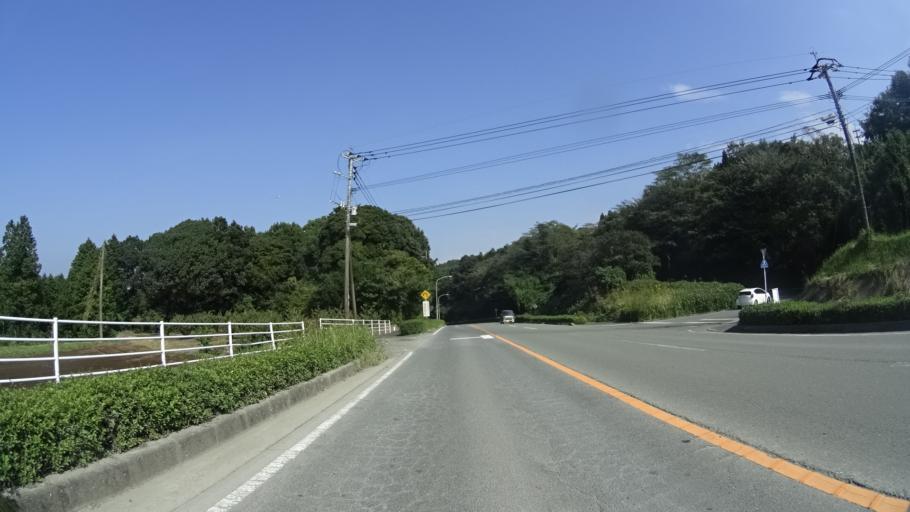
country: JP
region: Kumamoto
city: Ozu
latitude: 32.8465
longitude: 130.8593
